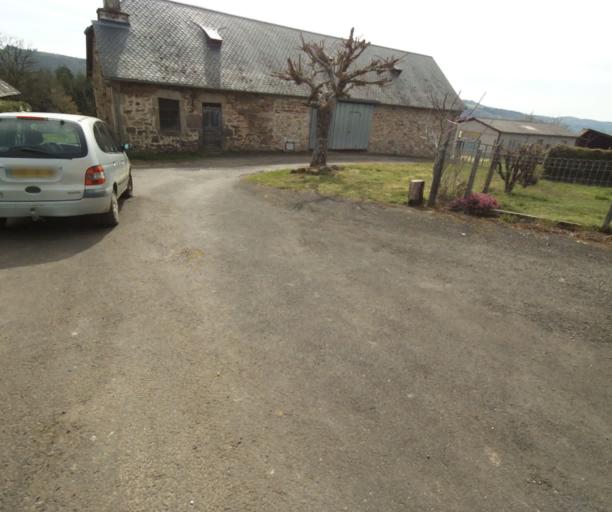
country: FR
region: Limousin
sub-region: Departement de la Correze
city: Correze
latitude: 45.3696
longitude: 1.8218
